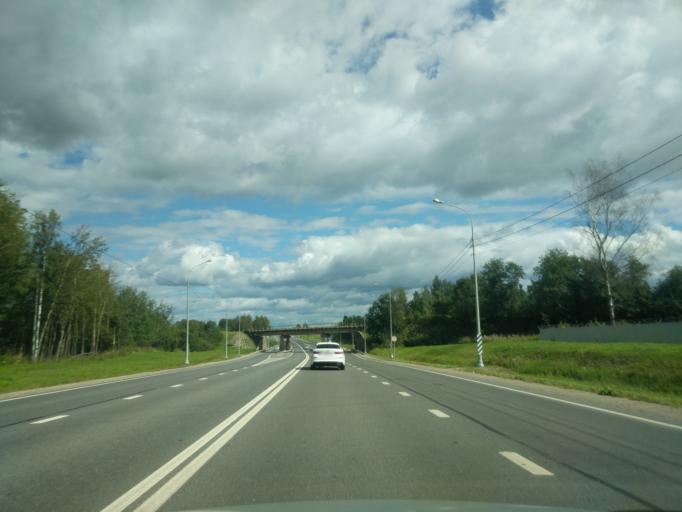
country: RU
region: Kostroma
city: Oktyabr'skiy
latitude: 57.7855
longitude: 41.0554
